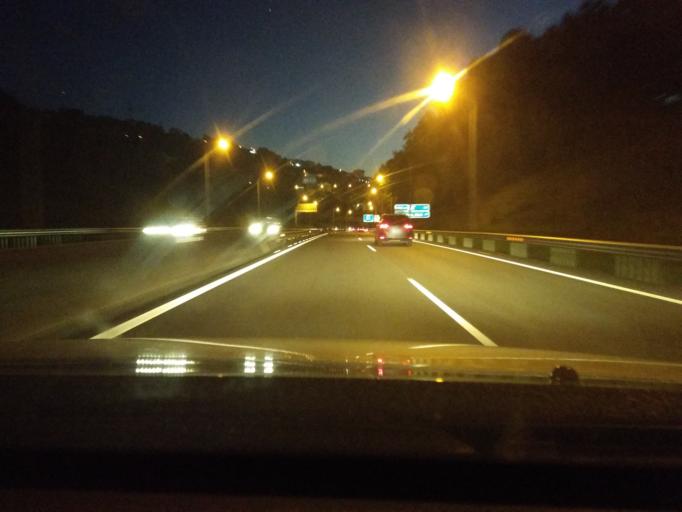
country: ES
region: Galicia
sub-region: Provincia de Pontevedra
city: Vigo
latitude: 42.2526
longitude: -8.6847
